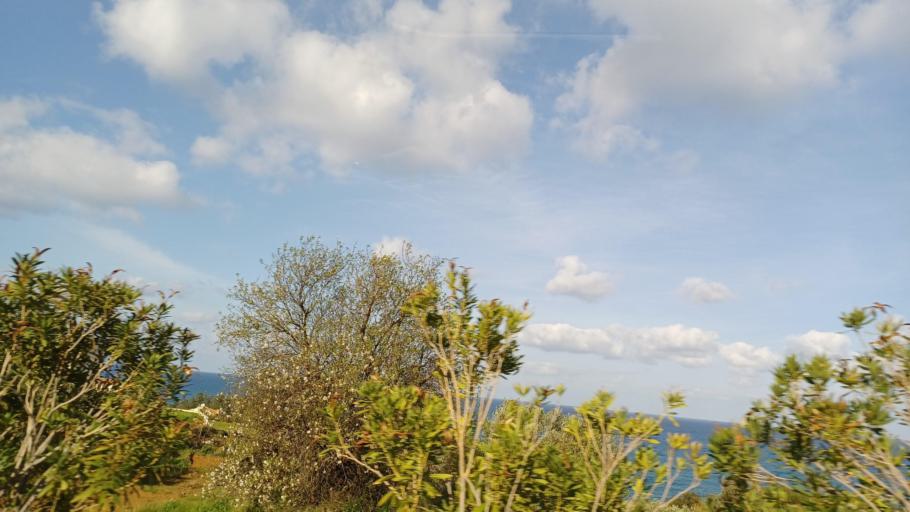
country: CY
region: Pafos
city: Polis
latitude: 35.1441
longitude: 32.5287
